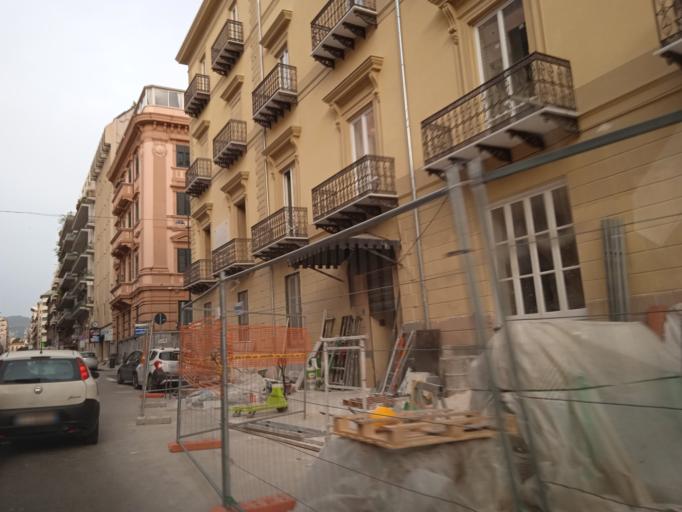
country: IT
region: Sicily
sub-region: Palermo
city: Palermo
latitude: 38.1236
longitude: 13.3593
